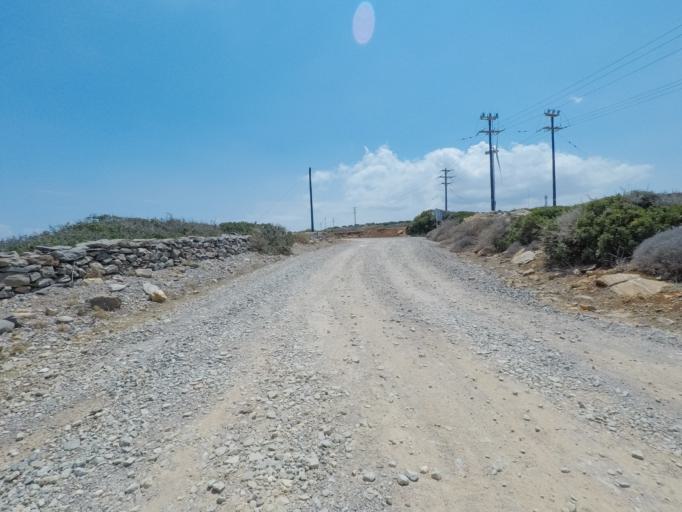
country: GR
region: Crete
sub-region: Nomos Lasithiou
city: Elounda
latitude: 35.3249
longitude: 25.7549
